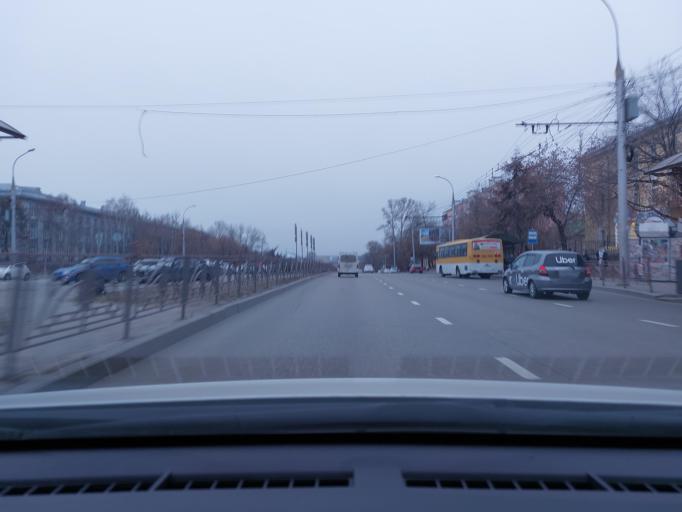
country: RU
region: Irkutsk
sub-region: Irkutskiy Rayon
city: Irkutsk
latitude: 52.2625
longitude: 104.2599
